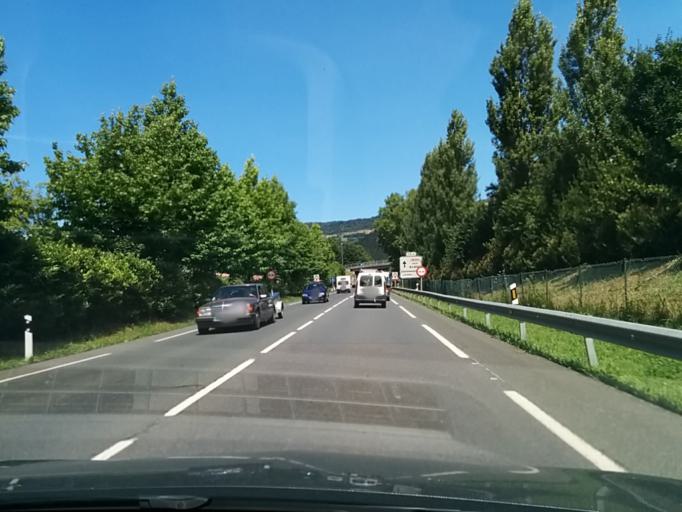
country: ES
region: Basque Country
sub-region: Provincia de Guipuzcoa
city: Usurbil
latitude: 43.2699
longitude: -2.0528
